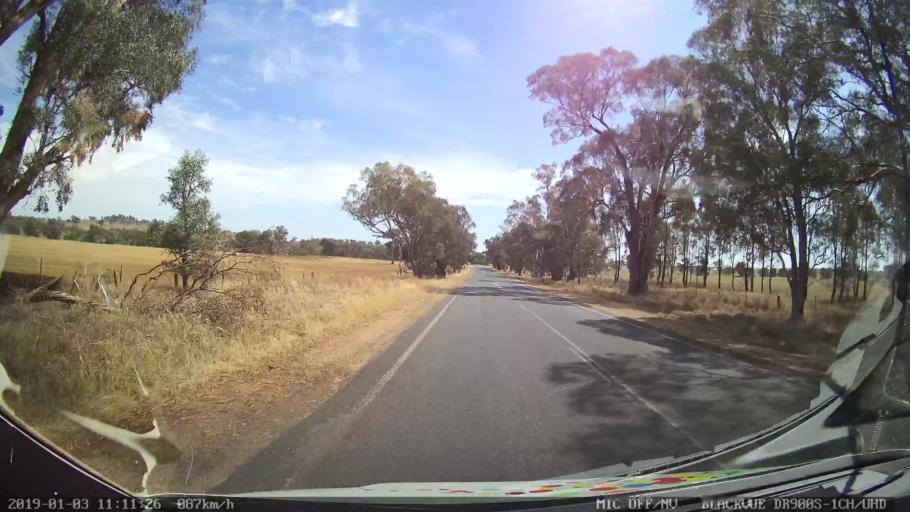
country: AU
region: New South Wales
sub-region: Young
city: Young
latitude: -34.2147
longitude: 148.2599
